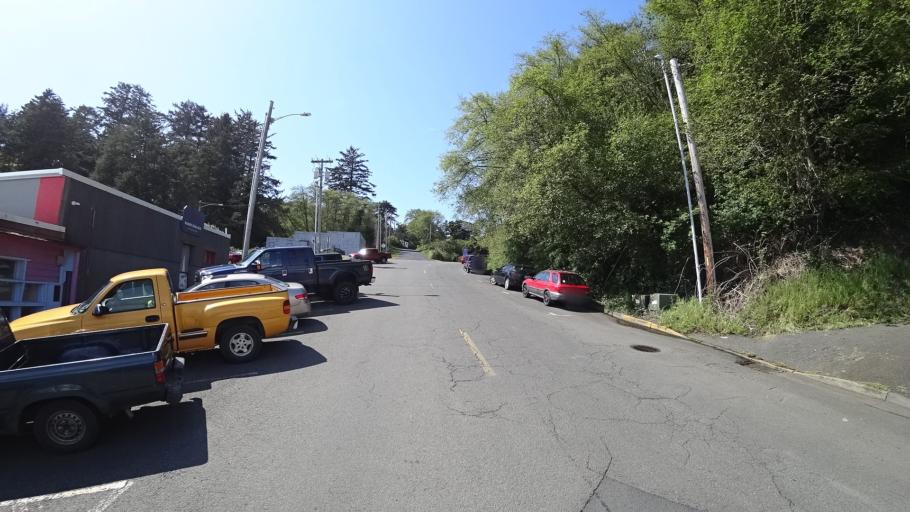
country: US
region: Oregon
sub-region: Lincoln County
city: Newport
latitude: 44.6295
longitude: -124.0548
